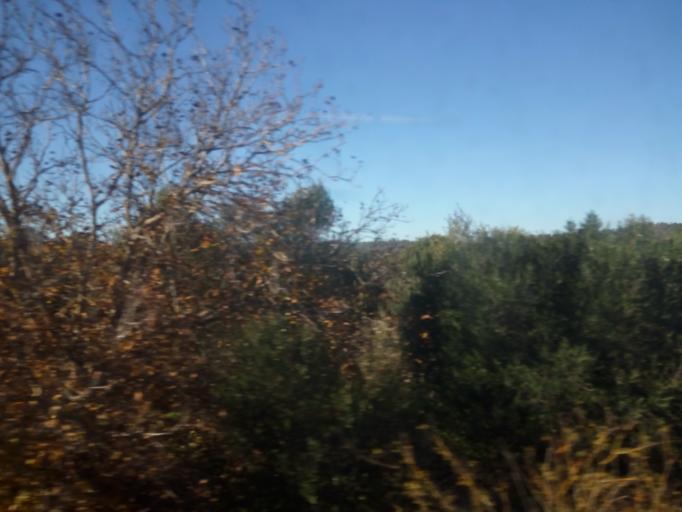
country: PT
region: Faro
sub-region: Loule
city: Boliqueime
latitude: 37.1176
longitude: -8.1687
